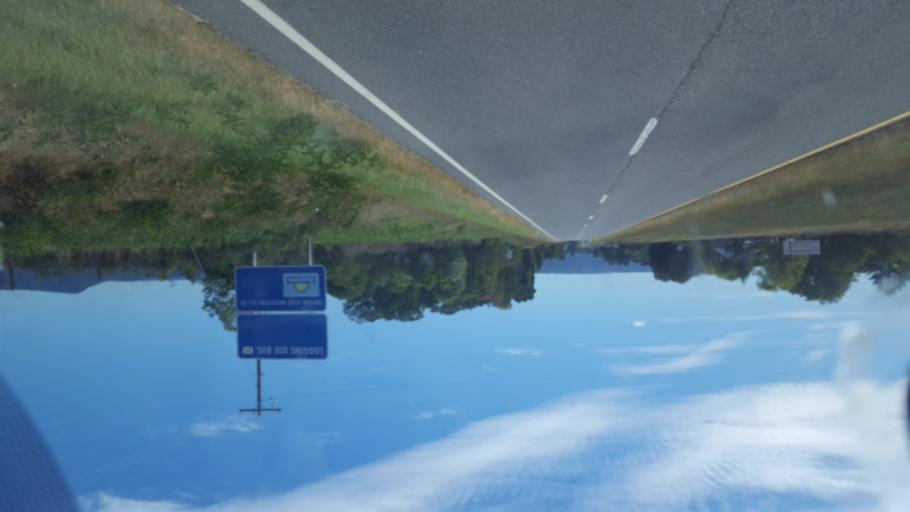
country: US
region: Virginia
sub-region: Page County
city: Luray
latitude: 38.6741
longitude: -78.3958
